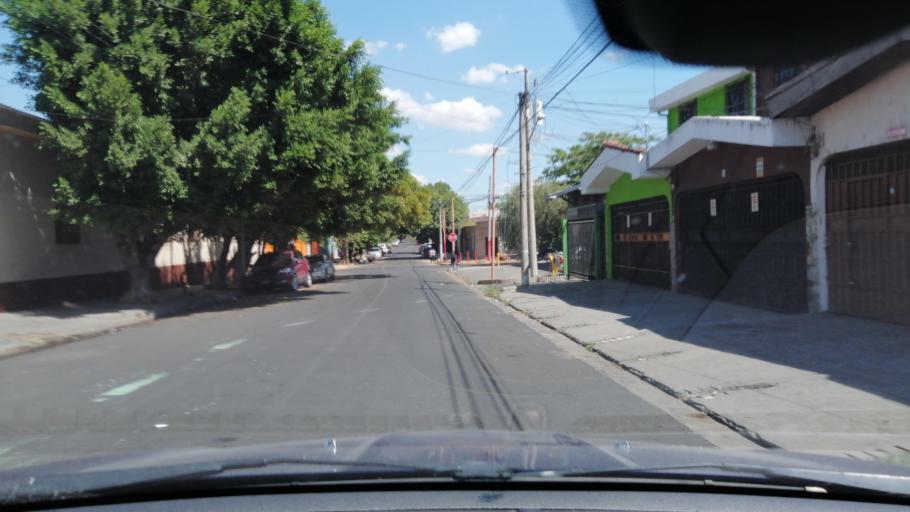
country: SV
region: Santa Ana
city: Santa Ana
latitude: 13.9848
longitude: -89.5582
